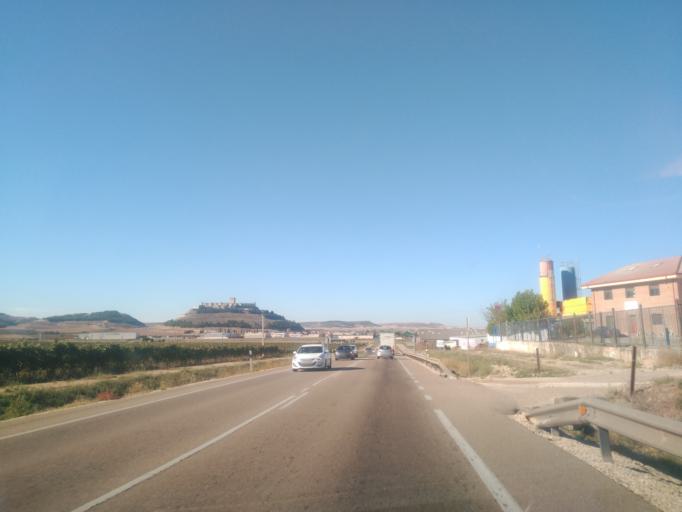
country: ES
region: Castille and Leon
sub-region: Provincia de Valladolid
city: Penafiel
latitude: 41.6100
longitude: -4.1003
